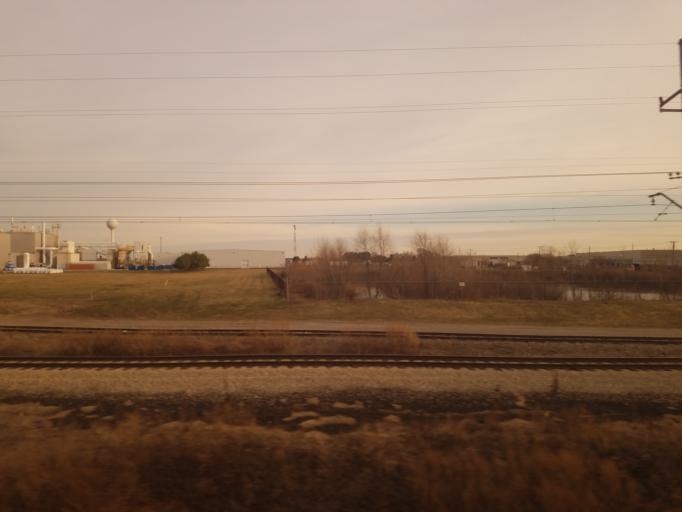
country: US
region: Indiana
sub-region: Saint Joseph County
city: New Carlisle
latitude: 41.7004
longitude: -86.4493
